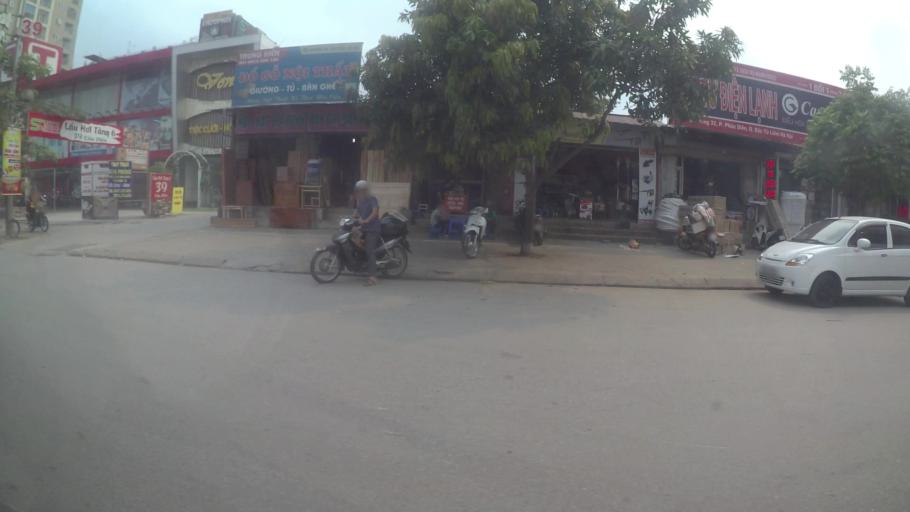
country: VN
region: Ha Noi
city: Cau Dien
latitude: 21.0427
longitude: 105.7582
